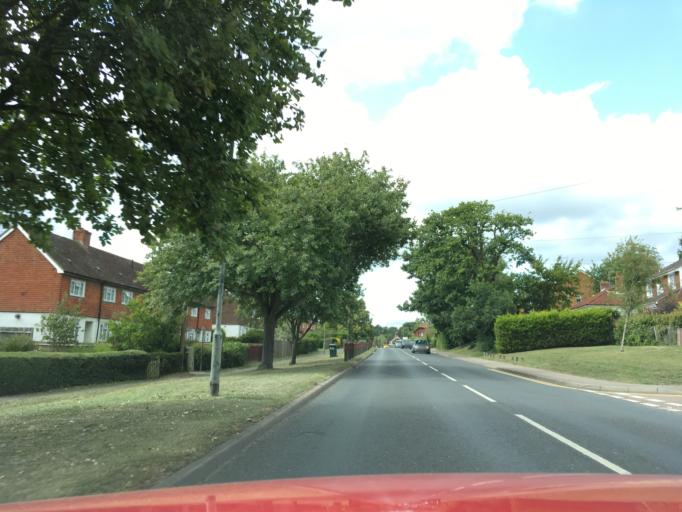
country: GB
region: England
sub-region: Kent
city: Tenterden
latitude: 51.0821
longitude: 0.6940
